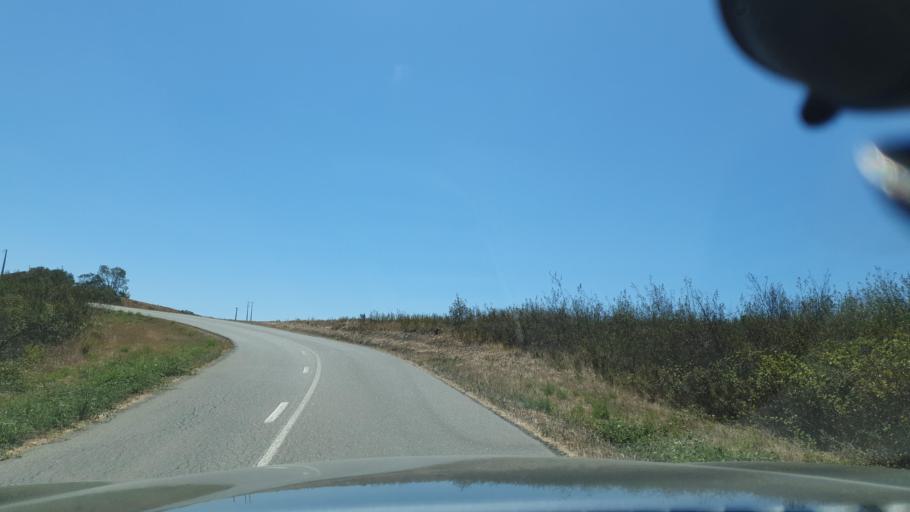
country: PT
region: Beja
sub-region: Odemira
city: Odemira
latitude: 37.5529
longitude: -8.4425
